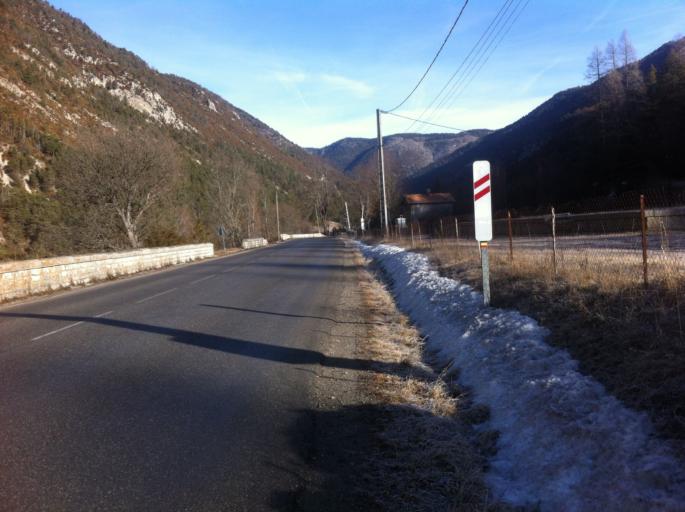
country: FR
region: Provence-Alpes-Cote d'Azur
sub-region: Departement des Alpes-de-Haute-Provence
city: Annot
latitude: 44.0421
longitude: 6.5645
